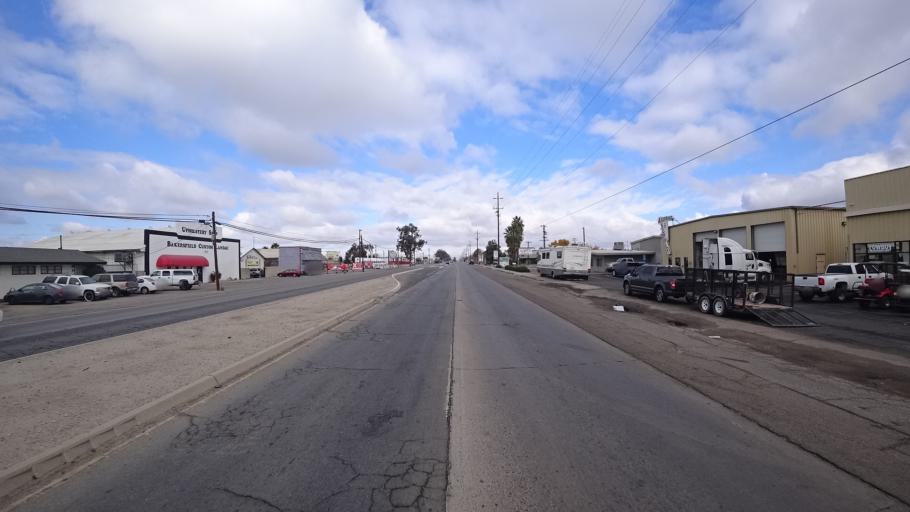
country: US
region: California
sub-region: Kern County
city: Bakersfield
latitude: 35.3340
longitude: -119.0030
